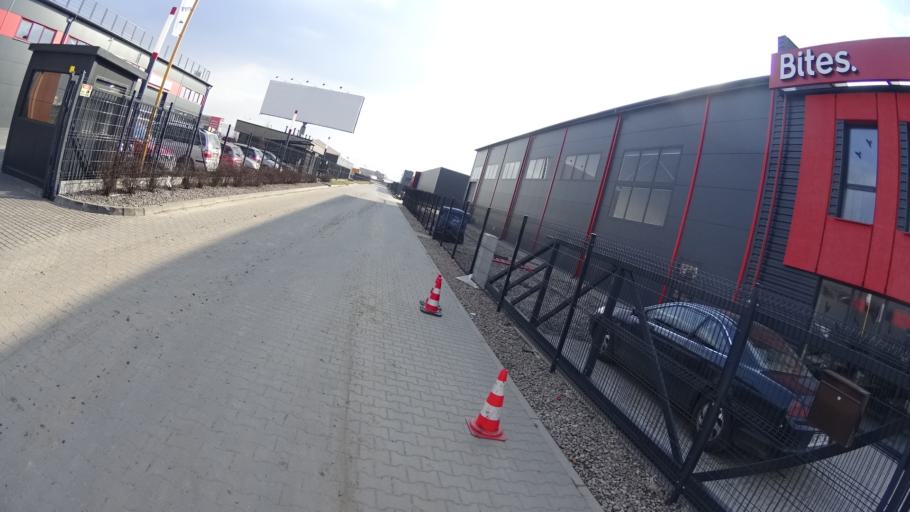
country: PL
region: Masovian Voivodeship
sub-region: Warszawa
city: Bemowo
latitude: 52.2348
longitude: 20.8815
